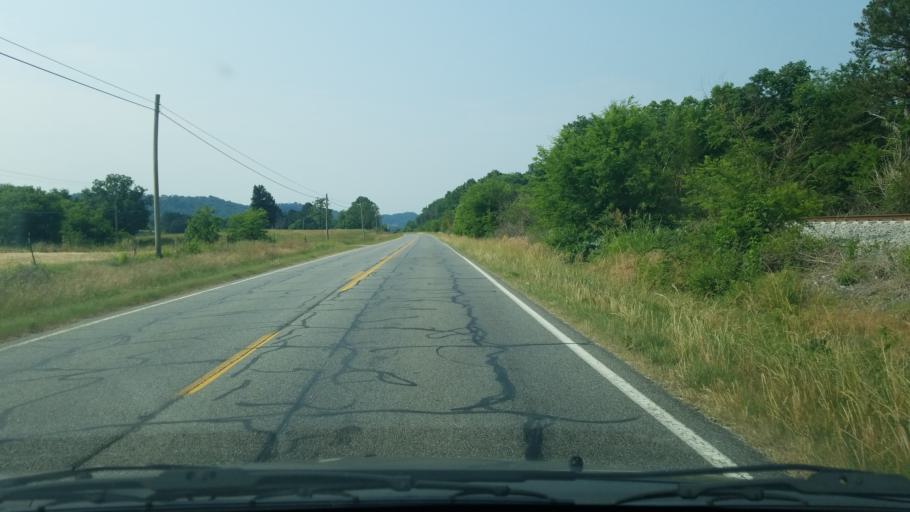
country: US
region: Georgia
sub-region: Catoosa County
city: Ringgold
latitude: 34.9480
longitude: -85.1042
